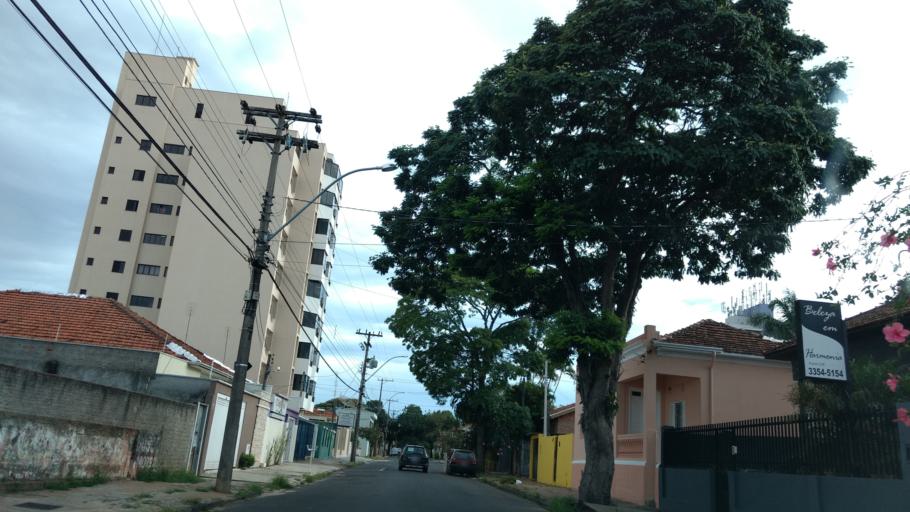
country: BR
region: Sao Paulo
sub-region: Botucatu
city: Botucatu
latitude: -22.8938
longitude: -48.4431
